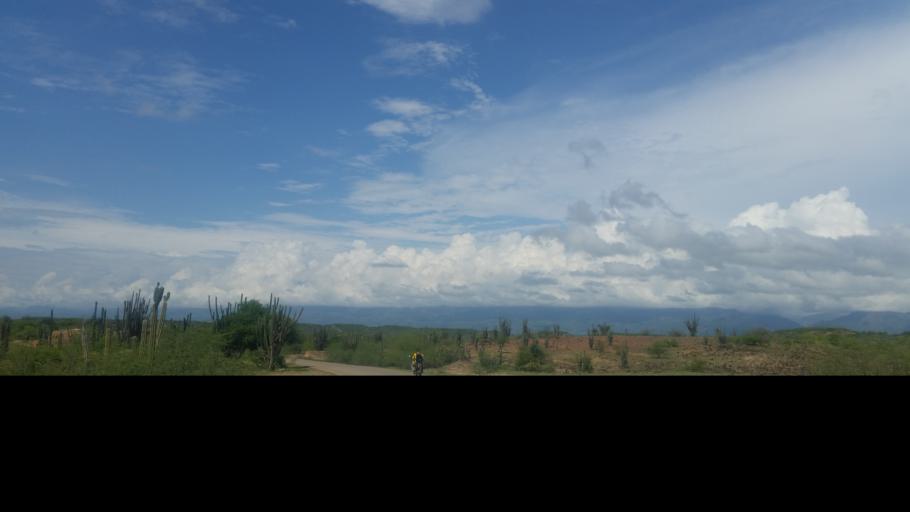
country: CO
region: Huila
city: Villavieja
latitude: 3.2312
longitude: -75.1787
